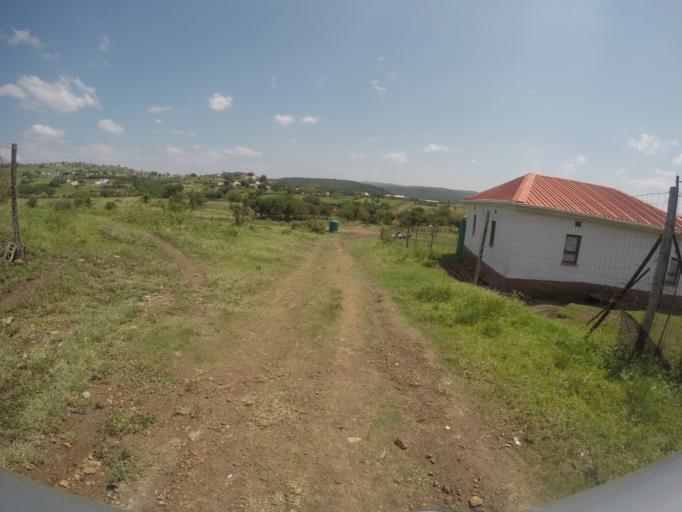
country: ZA
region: KwaZulu-Natal
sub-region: uThungulu District Municipality
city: Empangeni
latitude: -28.5959
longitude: 31.7363
